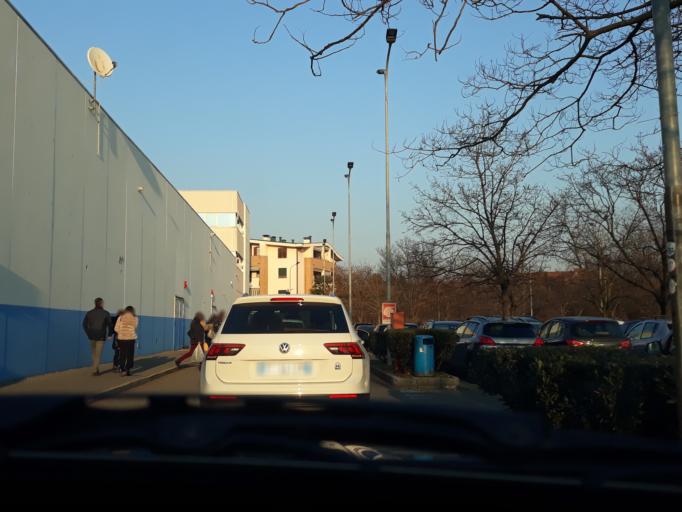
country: IT
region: Lombardy
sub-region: Provincia di Monza e Brianza
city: Lissone
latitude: 45.6050
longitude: 9.2288
